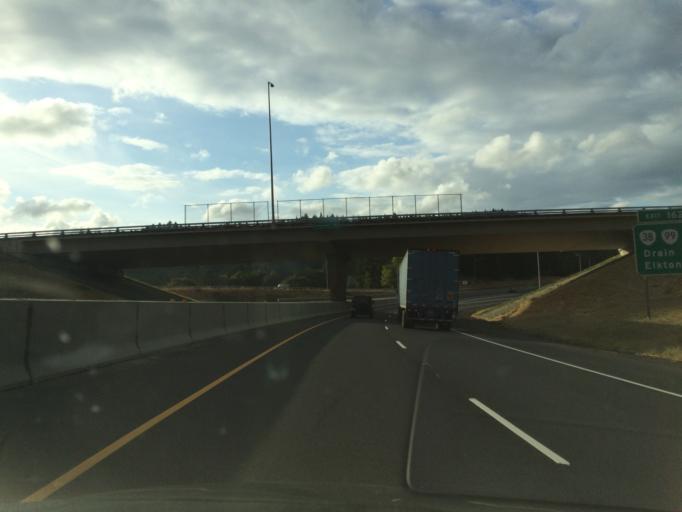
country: US
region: Oregon
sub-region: Douglas County
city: Drain
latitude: 43.7082
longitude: -123.2167
